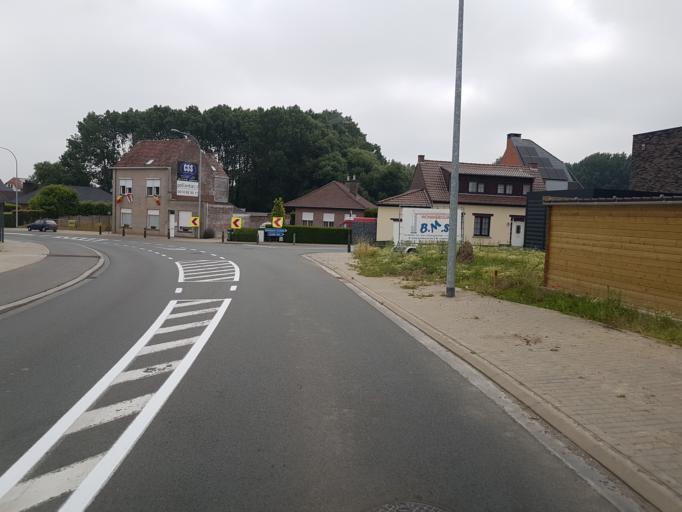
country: BE
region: Flanders
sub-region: Provincie Vlaams-Brabant
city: Galmaarden
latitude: 50.8237
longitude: 3.9442
